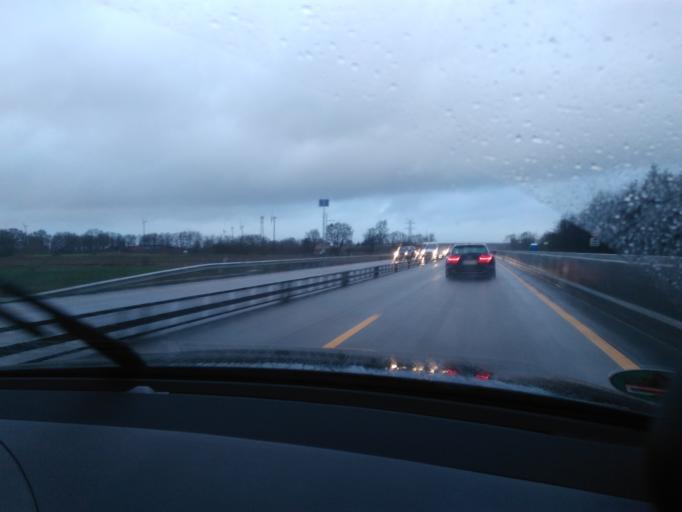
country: DE
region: Schleswig-Holstein
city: Bimohlen
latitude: 53.9496
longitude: 9.9495
